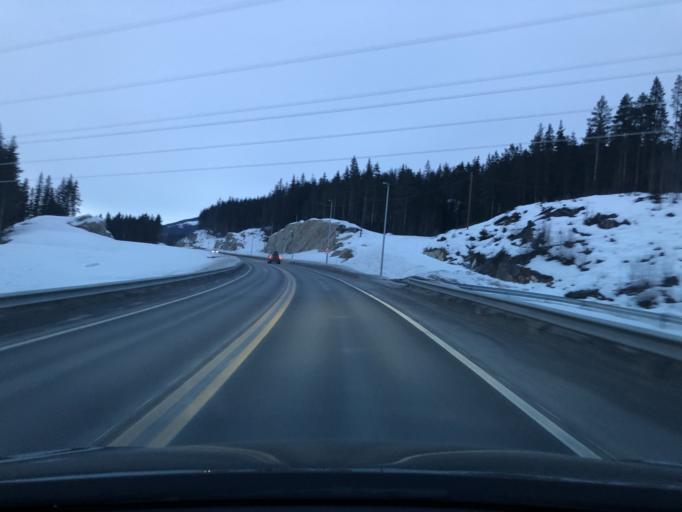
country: NO
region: Oppland
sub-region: Sor-Aurdal
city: Bagn
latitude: 60.8662
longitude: 9.5044
